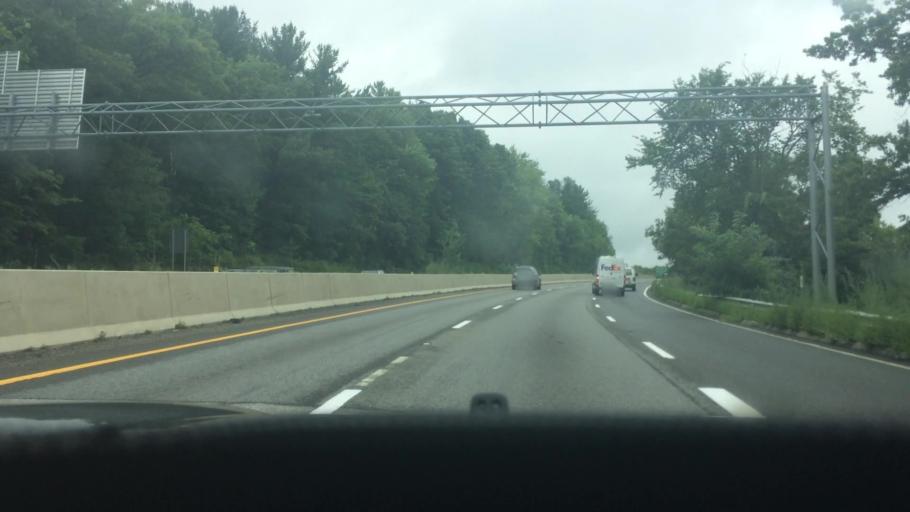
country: US
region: Massachusetts
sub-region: Worcester County
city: Leominster
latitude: 42.5473
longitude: -71.7628
